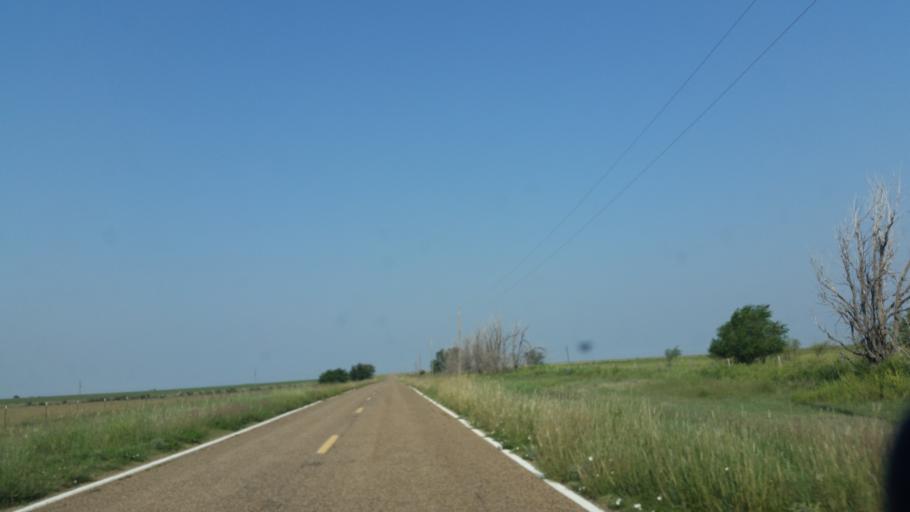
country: US
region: New Mexico
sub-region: Quay County
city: Logan
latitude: 34.9234
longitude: -103.3301
